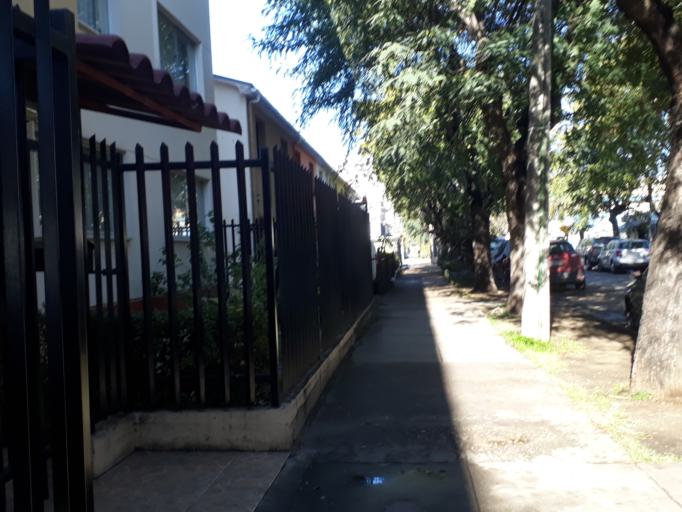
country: CL
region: Valparaiso
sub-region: Provincia de Valparaiso
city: Vina del Mar
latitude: -33.0121
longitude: -71.5455
